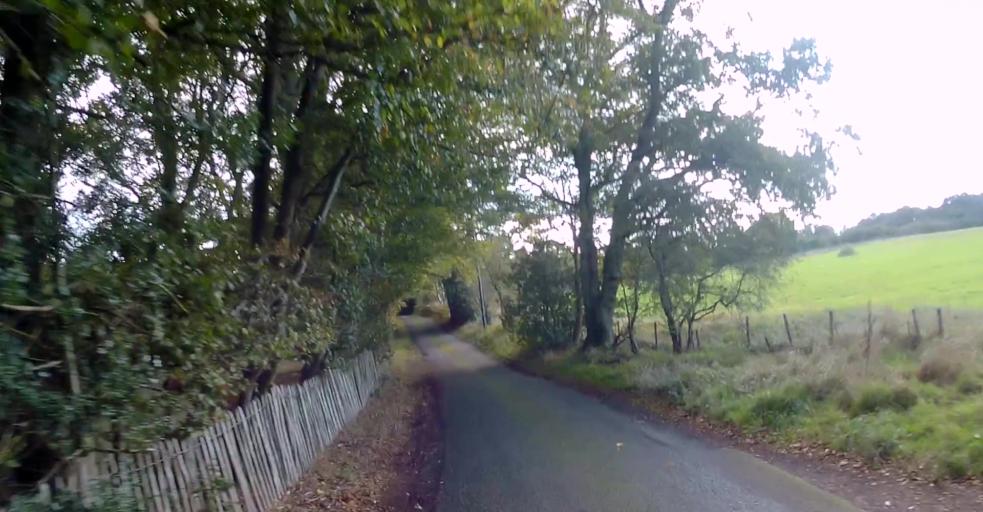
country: GB
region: England
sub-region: Surrey
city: Elstead
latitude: 51.1916
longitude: -0.7381
